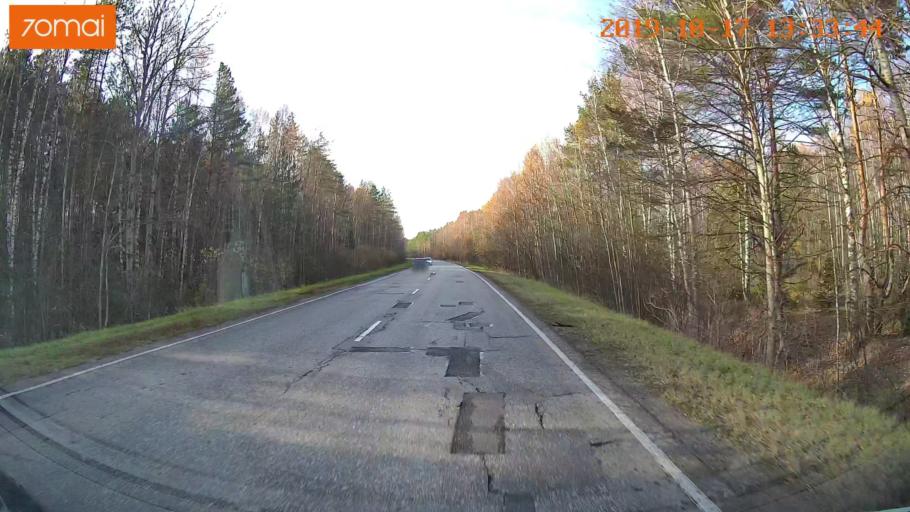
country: RU
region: Vladimir
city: Velikodvorskiy
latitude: 55.1440
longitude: 40.7343
